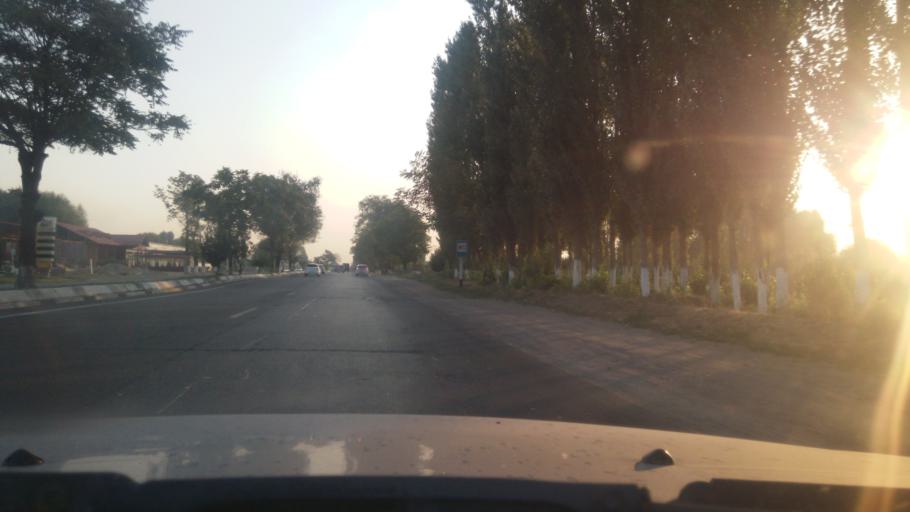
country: UZ
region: Toshkent
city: Yangiyul
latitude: 41.1732
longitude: 69.0690
